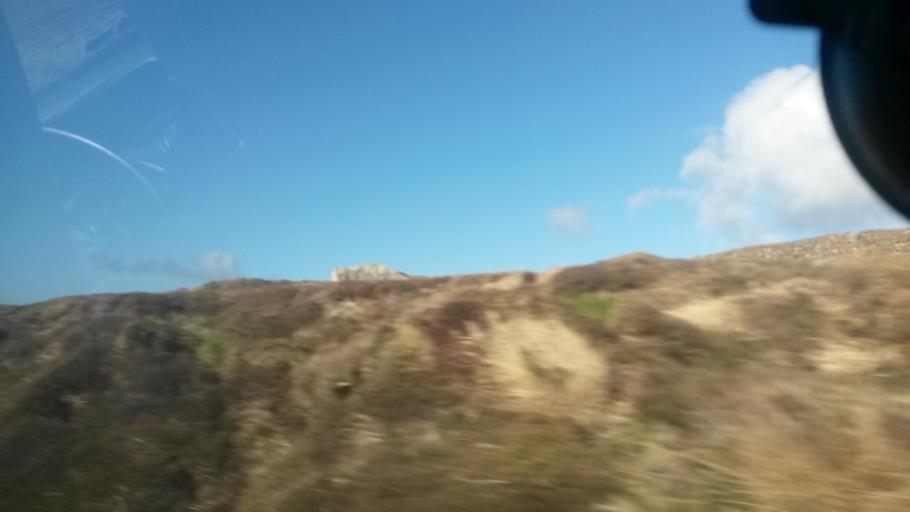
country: IE
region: Munster
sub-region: Ciarrai
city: Dingle
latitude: 52.1472
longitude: -10.4658
